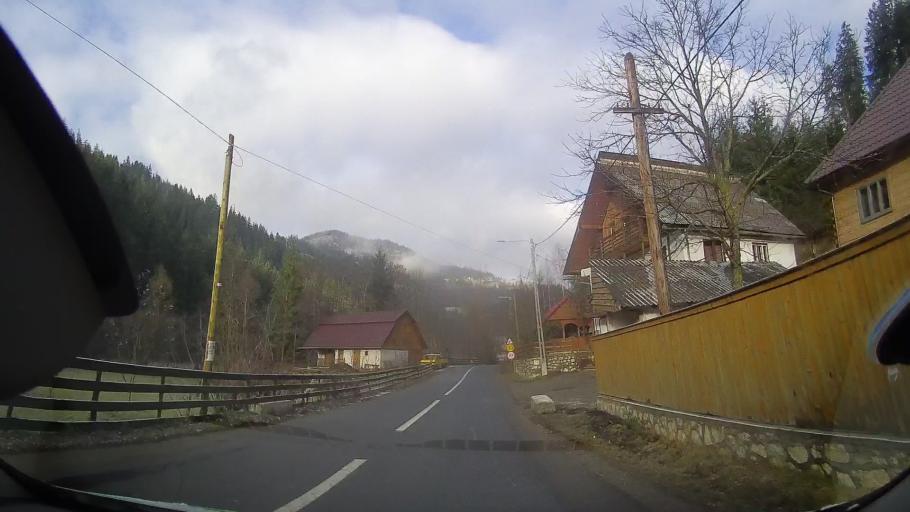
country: RO
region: Alba
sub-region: Comuna Albac
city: Albac
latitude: 46.4607
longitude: 22.9737
